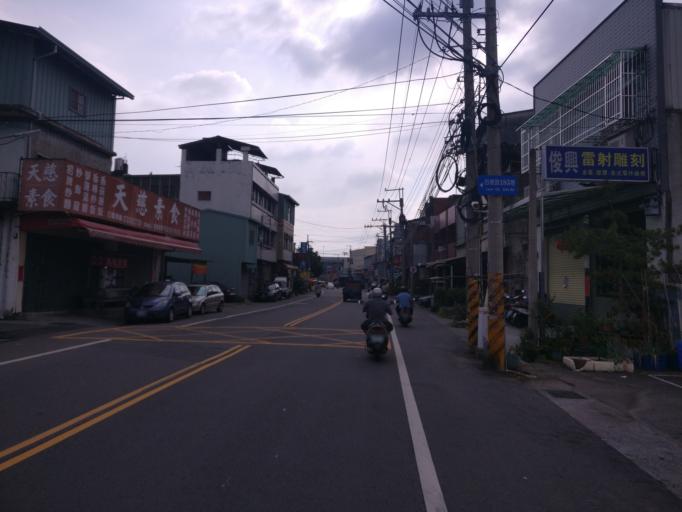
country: TW
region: Taiwan
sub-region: Taichung City
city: Taichung
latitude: 24.0661
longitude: 120.6935
